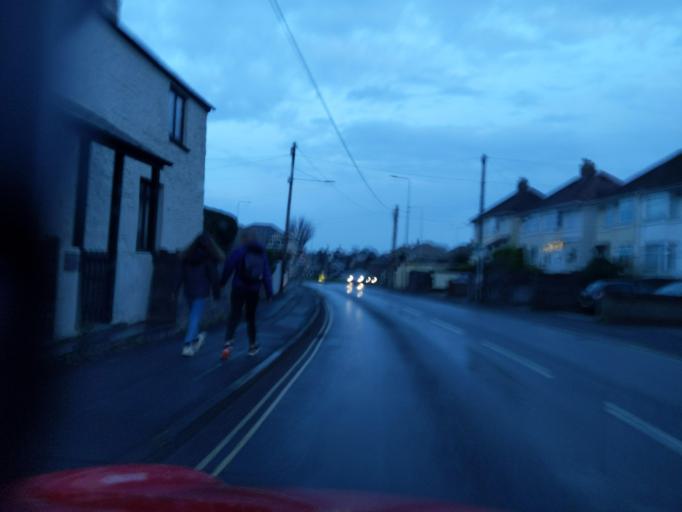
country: GB
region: England
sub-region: Plymouth
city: Plymstock
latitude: 50.3590
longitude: -4.0643
